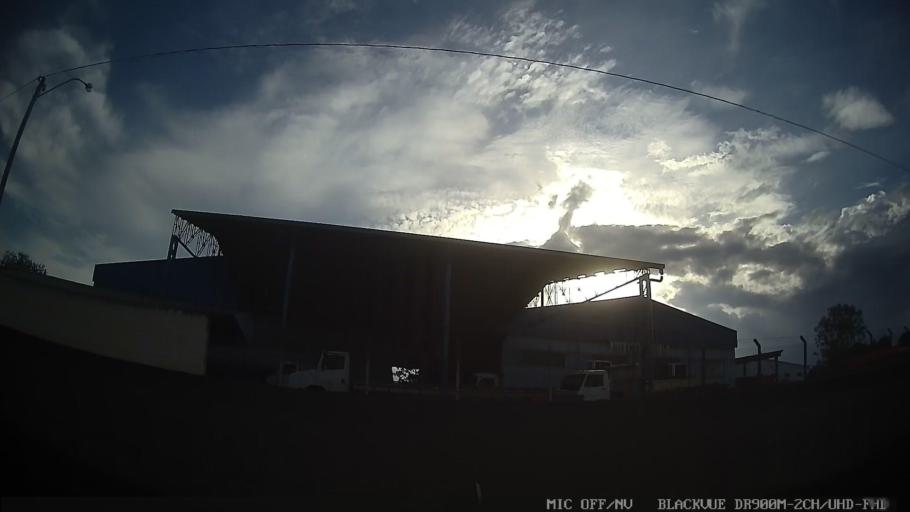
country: BR
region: Sao Paulo
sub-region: Tiete
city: Tiete
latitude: -23.0843
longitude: -47.7196
